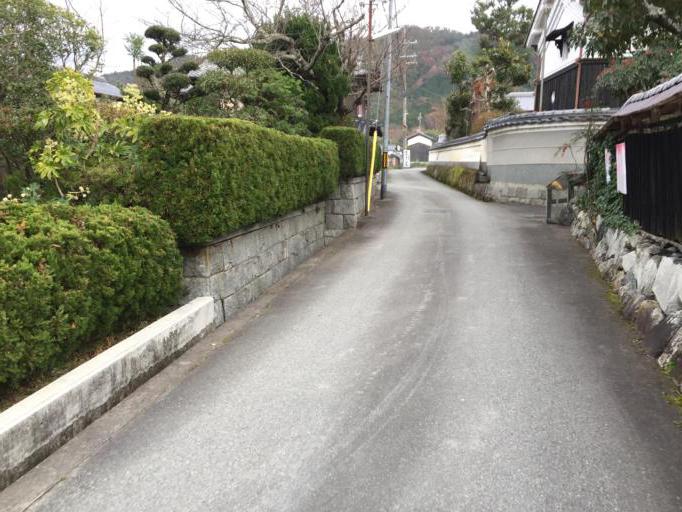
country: JP
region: Kyoto
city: Kameoka
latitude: 34.9902
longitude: 135.5478
